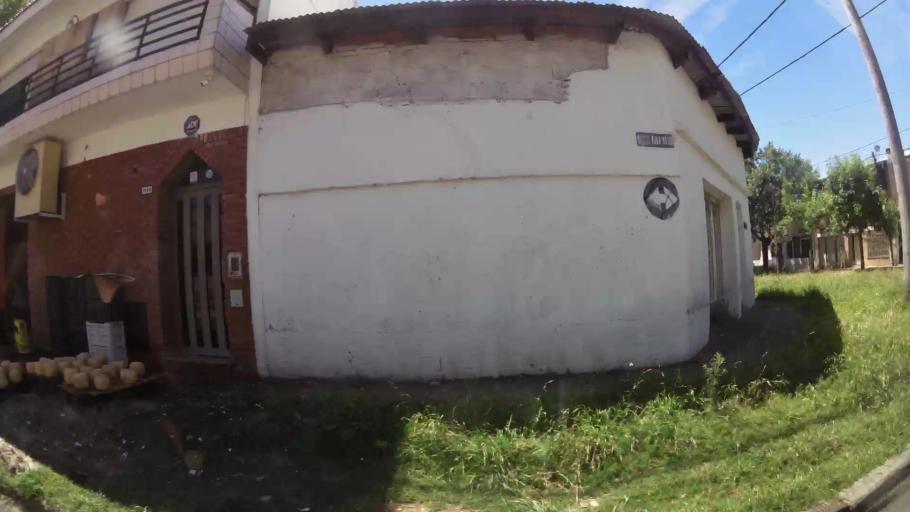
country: AR
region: Santa Fe
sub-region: Departamento de Rosario
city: Rosario
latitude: -32.9453
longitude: -60.7048
